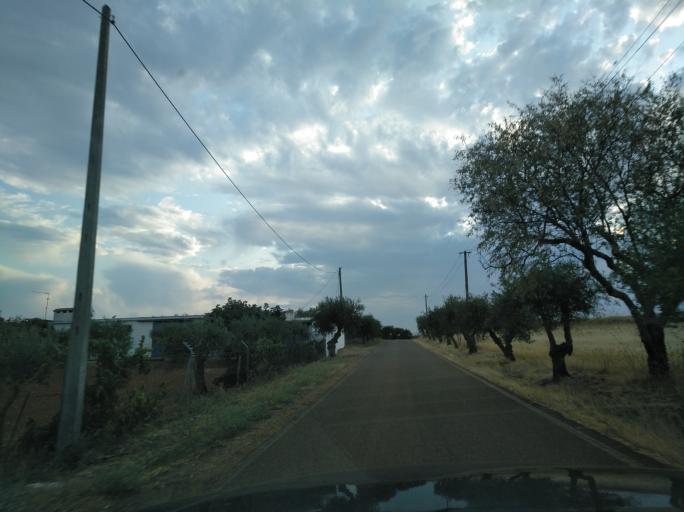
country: PT
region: Portalegre
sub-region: Campo Maior
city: Campo Maior
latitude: 39.0162
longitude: -7.0324
